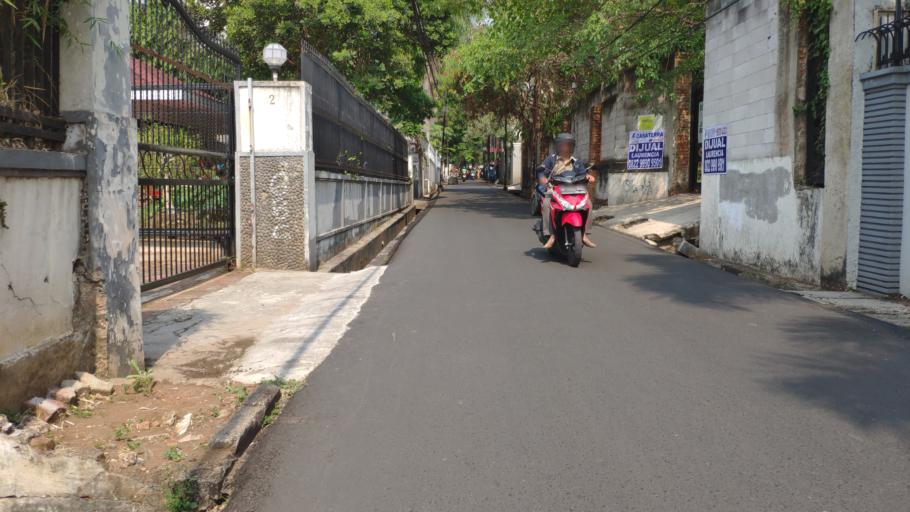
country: ID
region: Jakarta Raya
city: Jakarta
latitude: -6.2547
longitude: 106.8137
